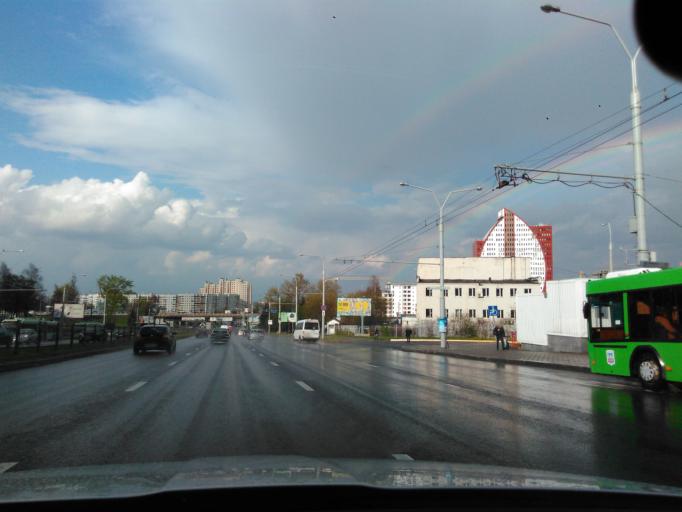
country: BY
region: Minsk
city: Novoye Medvezhino
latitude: 53.9235
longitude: 27.5027
